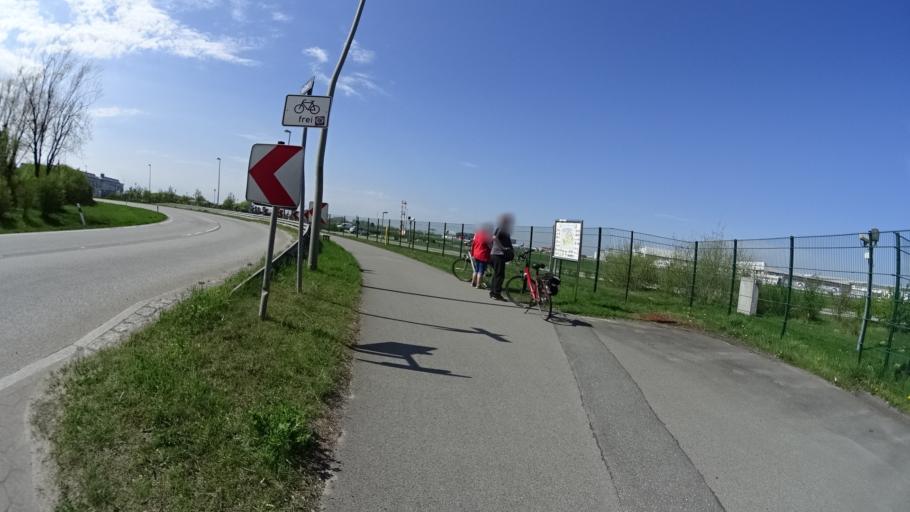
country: DE
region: Lower Saxony
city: Neu Wulmstorf
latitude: 53.5368
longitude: 9.8434
